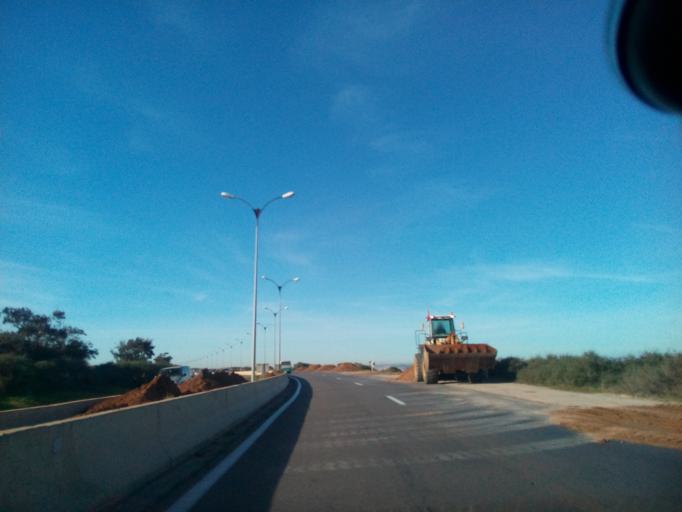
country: DZ
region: Mostaganem
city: Mostaganem
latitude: 35.8000
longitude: -0.0813
